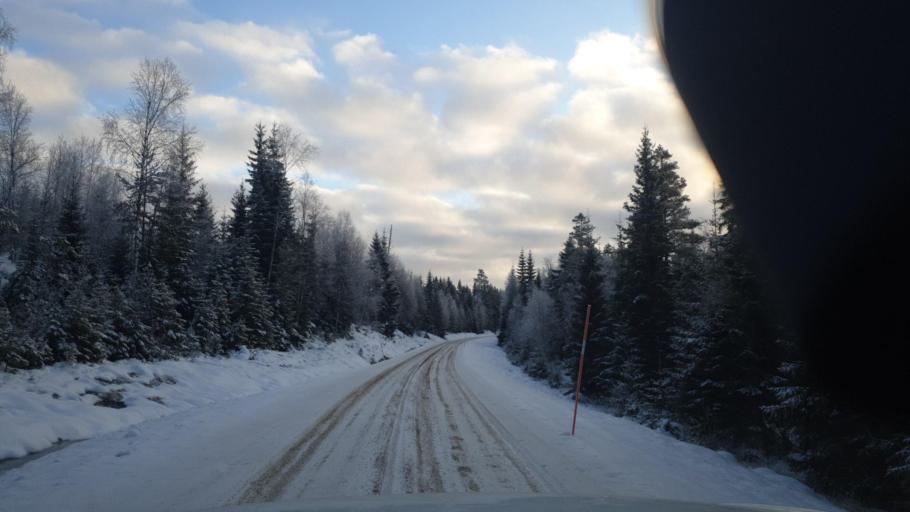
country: SE
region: Vaermland
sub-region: Eda Kommun
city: Charlottenberg
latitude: 60.1262
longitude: 12.5962
